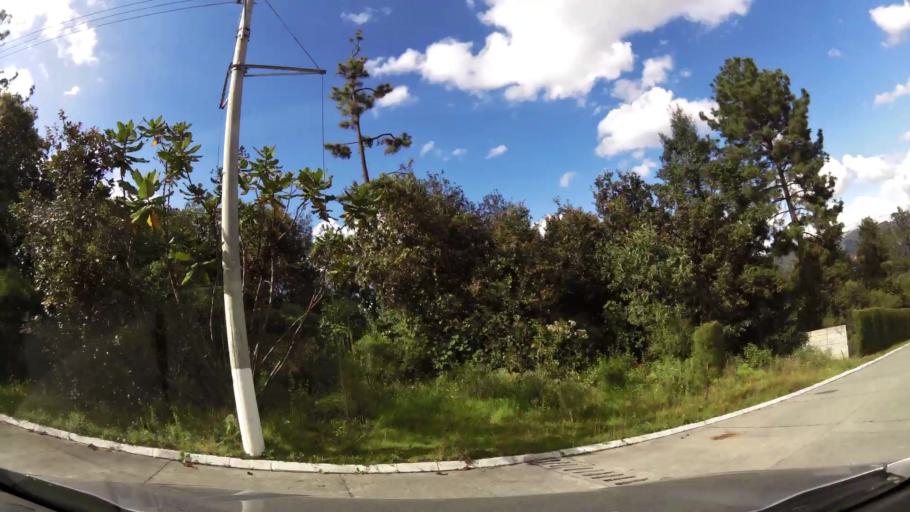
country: GT
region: Quetzaltenango
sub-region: Municipio de La Esperanza
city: La Esperanza
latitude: 14.8350
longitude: -91.5603
